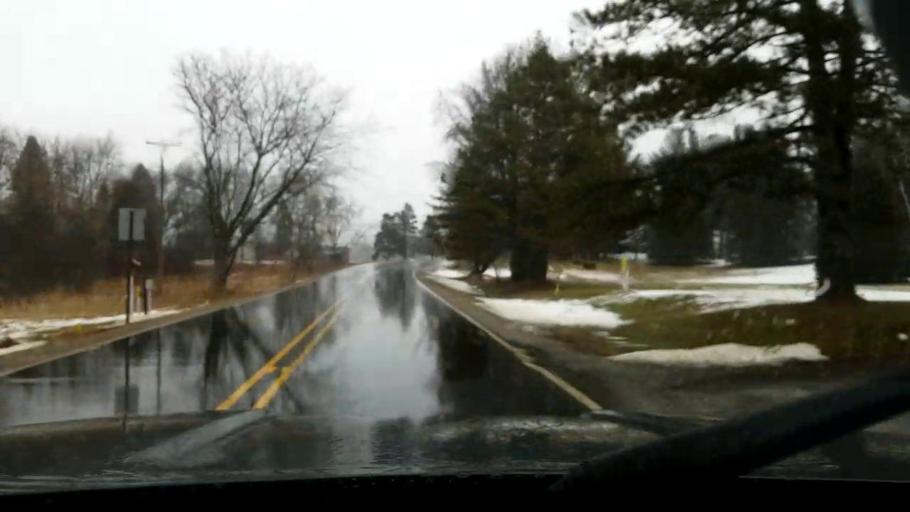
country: US
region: Michigan
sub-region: Jackson County
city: Michigan Center
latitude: 42.2979
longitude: -84.3170
